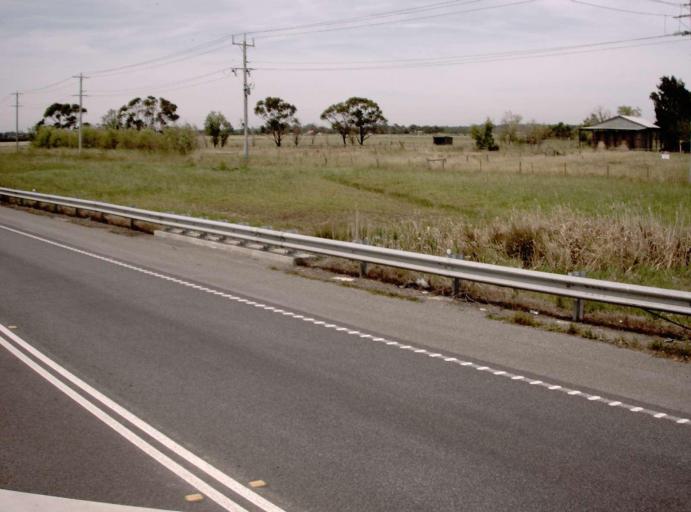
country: AU
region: Victoria
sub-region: Mornington Peninsula
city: Langwarrin South
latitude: -38.2149
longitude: 145.2192
